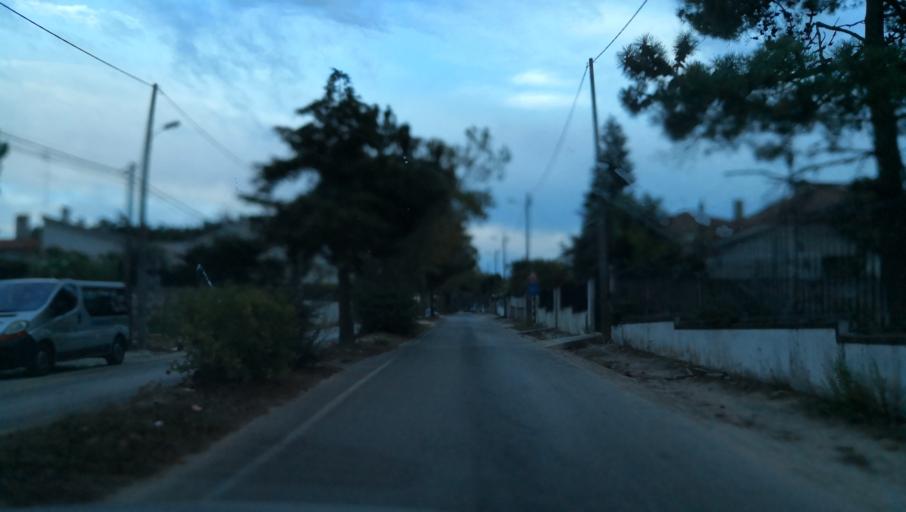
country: PT
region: Setubal
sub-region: Almada
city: Charneca
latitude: 38.6012
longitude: -9.1639
